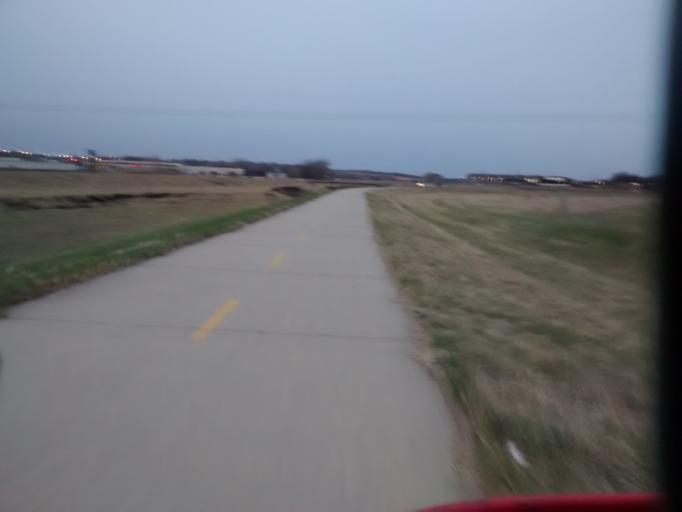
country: US
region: Nebraska
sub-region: Sarpy County
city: Offutt Air Force Base
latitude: 41.1443
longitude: -95.9610
